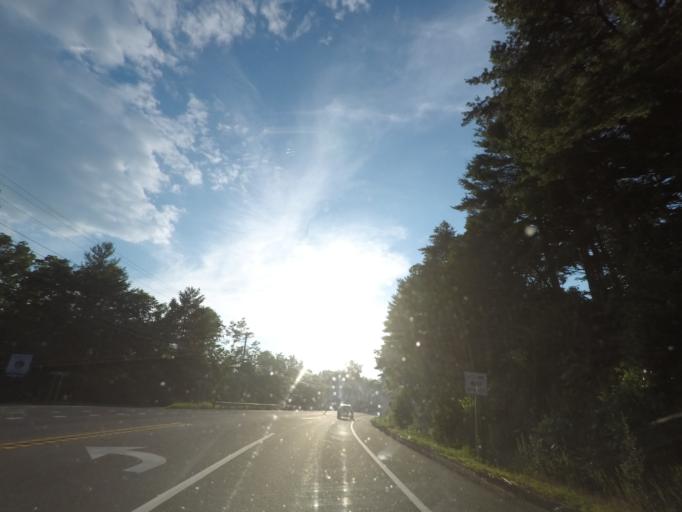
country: US
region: Massachusetts
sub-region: Worcester County
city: Fiskdale
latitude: 42.1111
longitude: -72.1474
